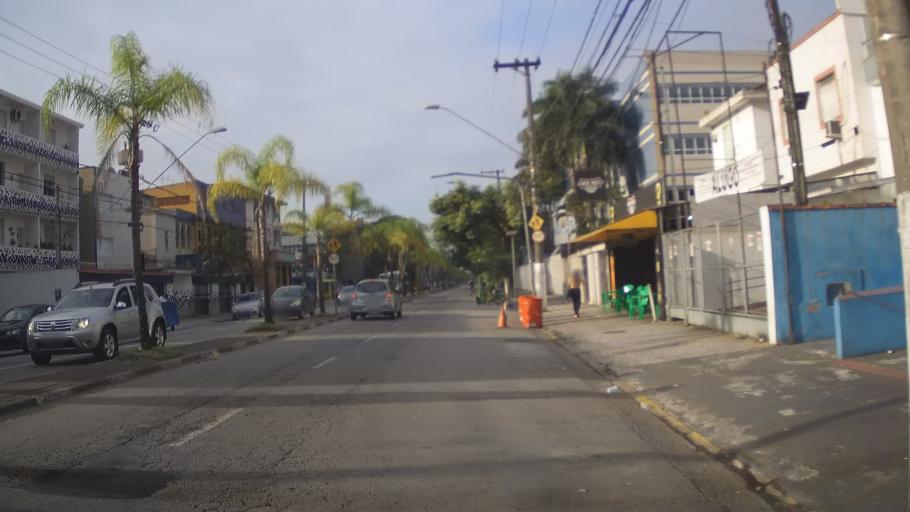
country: BR
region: Sao Paulo
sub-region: Santos
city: Santos
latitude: -23.9458
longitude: -46.3219
